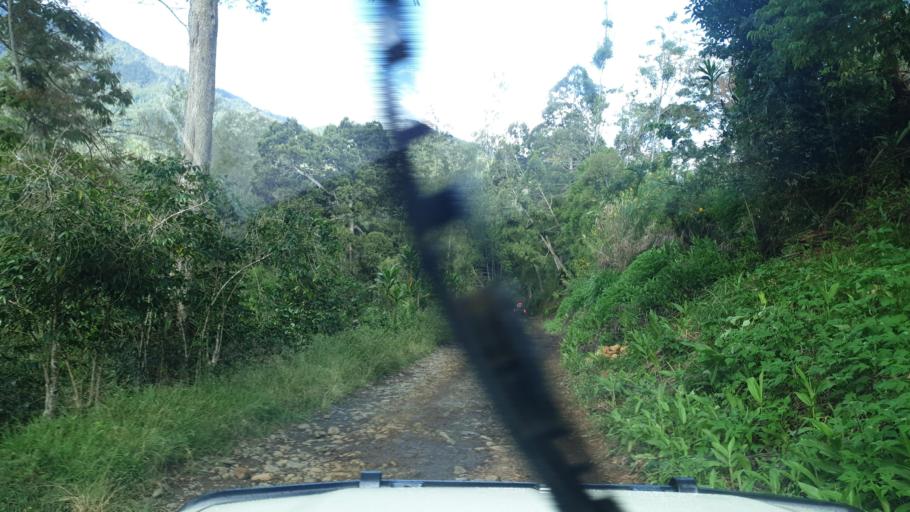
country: PG
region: Eastern Highlands
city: Goroka
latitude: -5.9202
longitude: 145.2586
